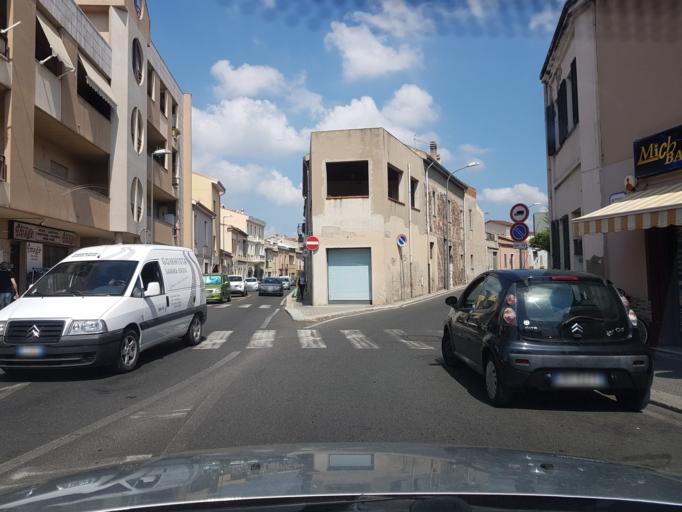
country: IT
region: Sardinia
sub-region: Provincia di Oristano
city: Oristano
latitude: 39.9027
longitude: 8.5991
